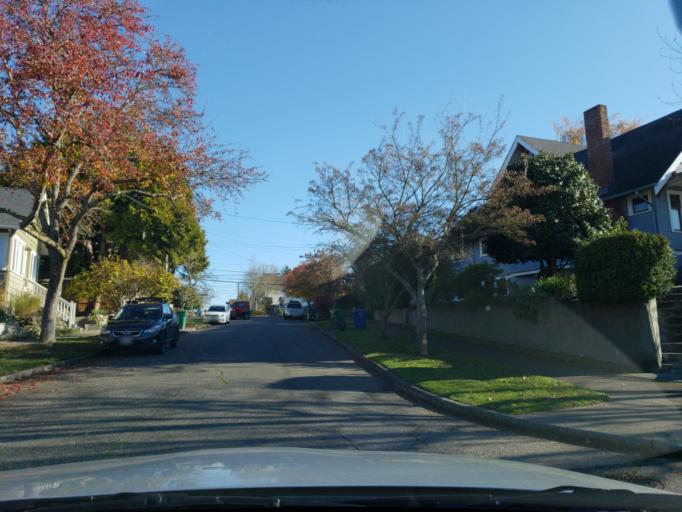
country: US
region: Washington
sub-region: King County
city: Seattle
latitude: 47.6740
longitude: -122.3564
